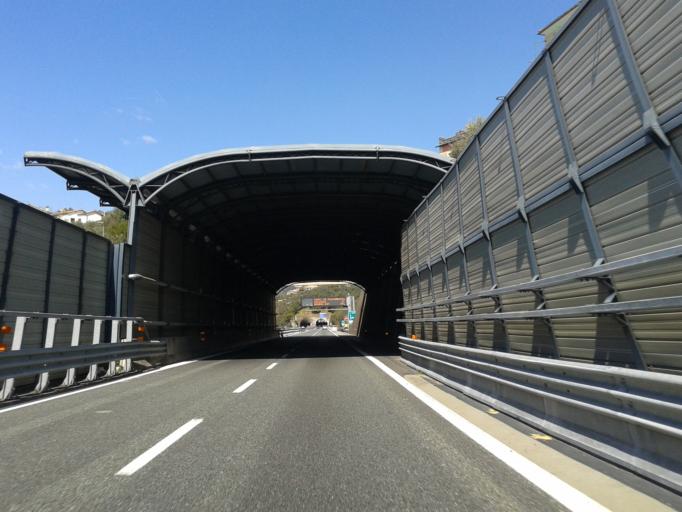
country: IT
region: Liguria
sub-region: Provincia di Genova
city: Lavagna
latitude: 44.3098
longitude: 9.3623
